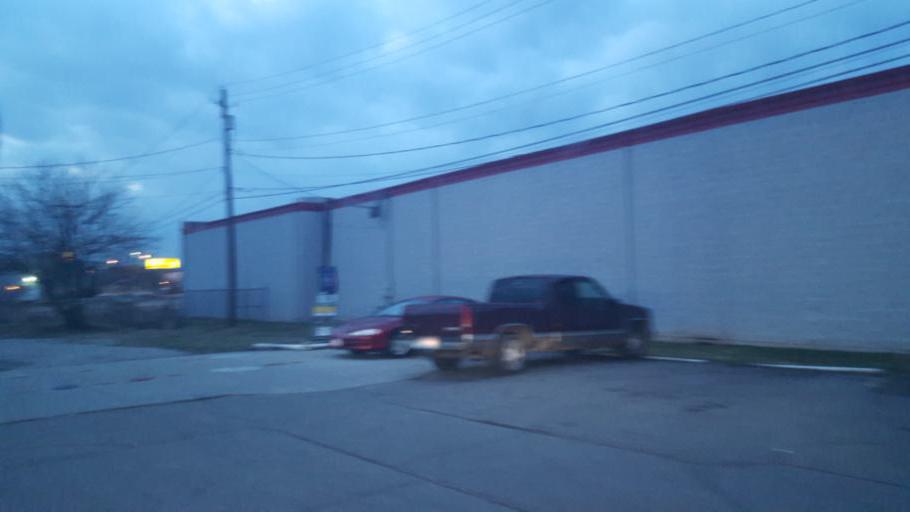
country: US
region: Ohio
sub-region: Ross County
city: Chillicothe
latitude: 39.3640
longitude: -82.9764
